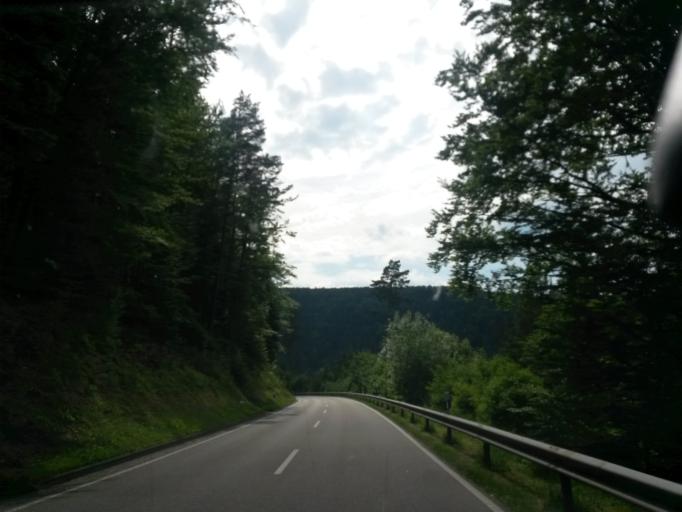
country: DE
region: Baden-Wuerttemberg
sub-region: Karlsruhe Region
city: Bad Liebenzell
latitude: 48.7460
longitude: 8.7380
